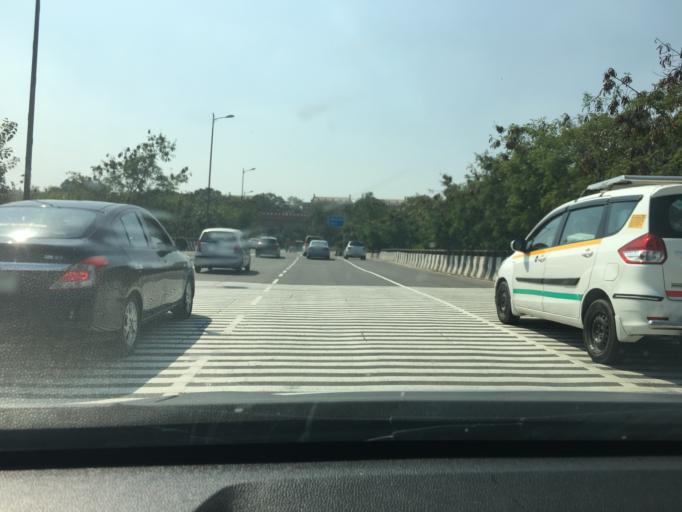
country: IN
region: NCT
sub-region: North Delhi
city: Delhi
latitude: 28.6595
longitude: 77.2459
